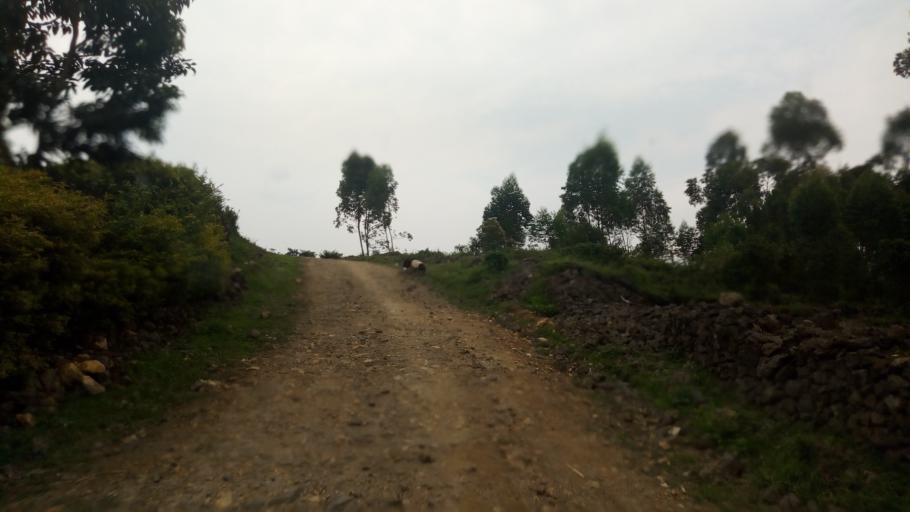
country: UG
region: Western Region
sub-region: Kisoro District
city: Kisoro
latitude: -1.2674
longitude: 29.6257
